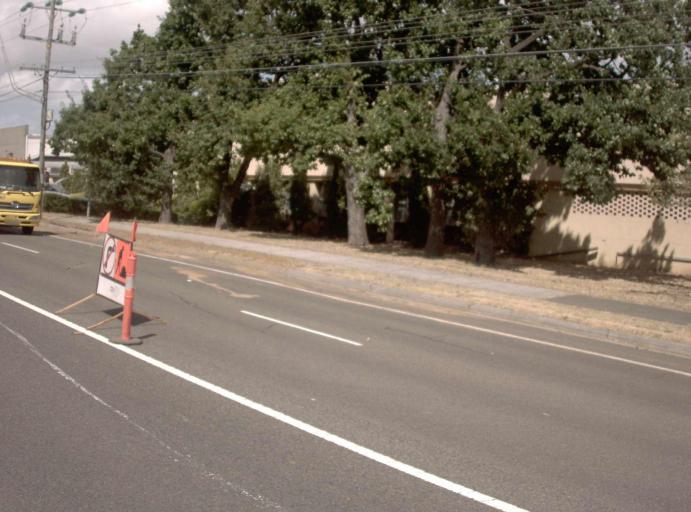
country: AU
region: Victoria
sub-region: Monash
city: Notting Hill
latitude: -37.8964
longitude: 145.1298
